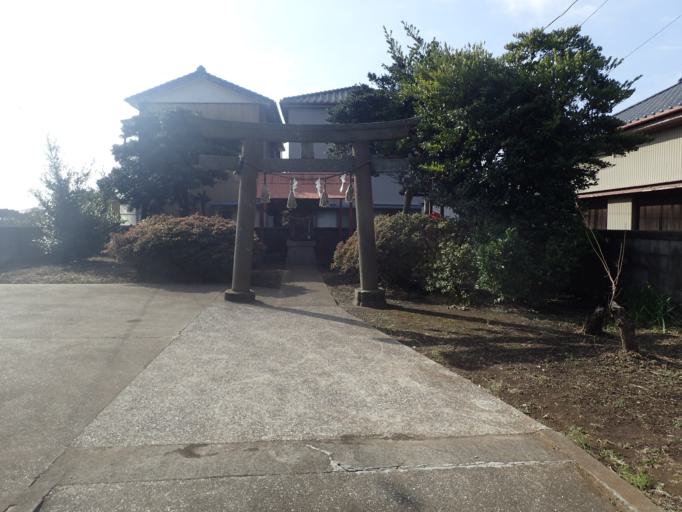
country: JP
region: Kanagawa
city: Miura
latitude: 35.1414
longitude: 139.6266
